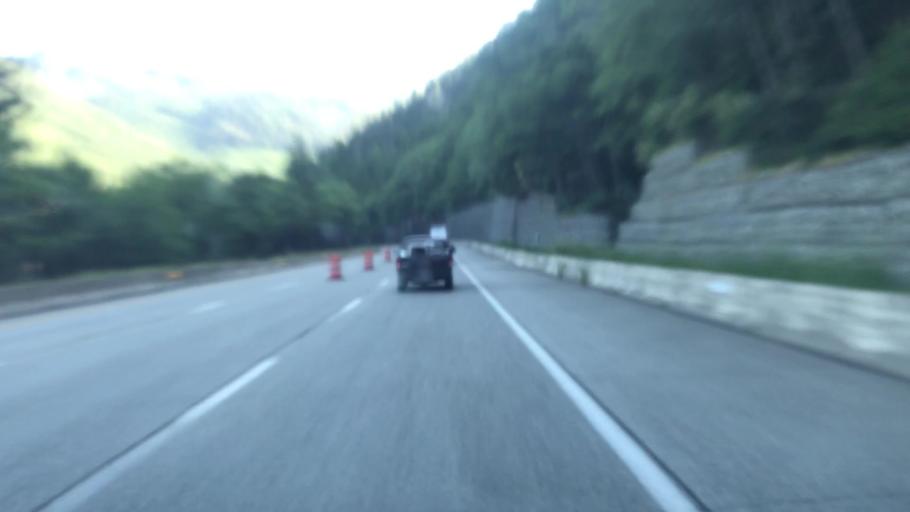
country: US
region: Washington
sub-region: King County
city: Tanner
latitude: 47.4120
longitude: -121.4468
